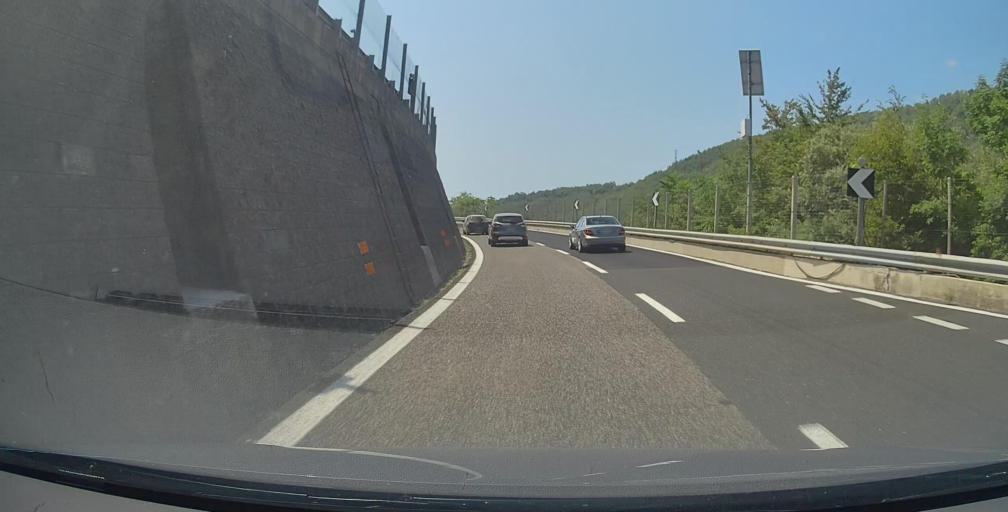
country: IT
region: Campania
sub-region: Provincia di Salerno
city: Vietri sul Mare
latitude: 40.6794
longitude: 14.7236
